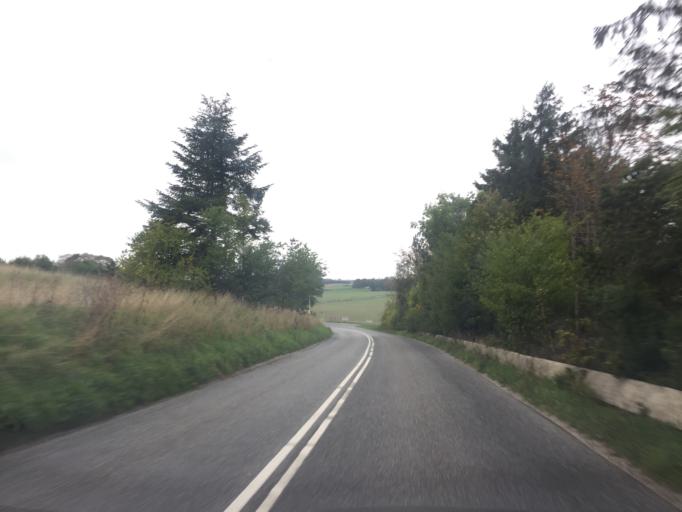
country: DK
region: Capital Region
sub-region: Hillerod Kommune
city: Skaevinge
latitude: 55.8855
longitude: 12.1506
